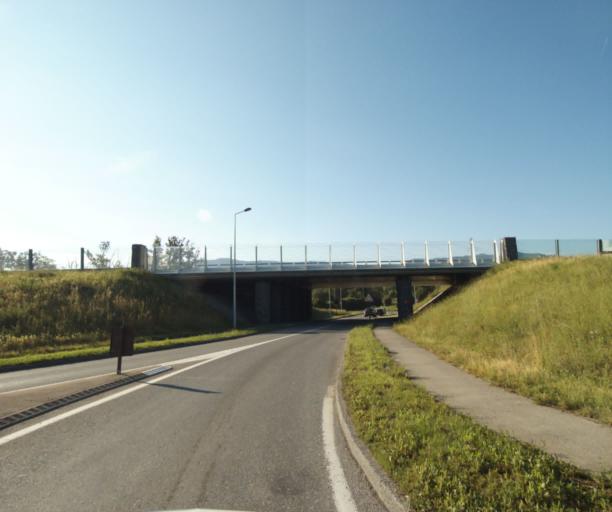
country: FR
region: Rhone-Alpes
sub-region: Departement de la Haute-Savoie
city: Allinges
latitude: 46.3525
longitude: 6.4587
